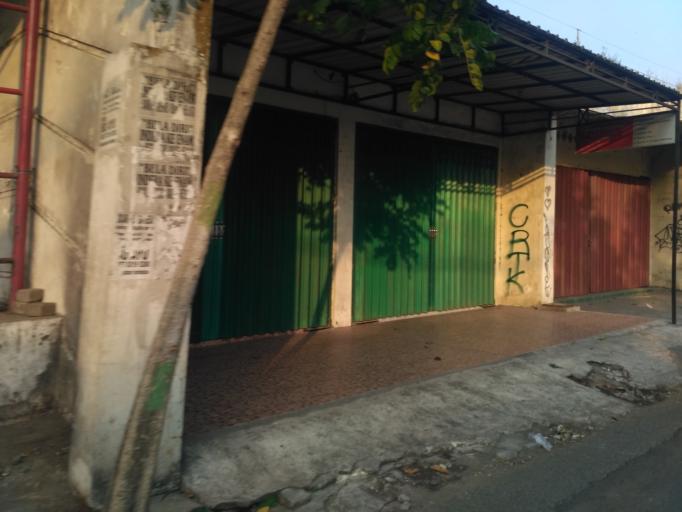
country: ID
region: East Java
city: Kepuh
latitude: -8.0093
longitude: 112.6197
